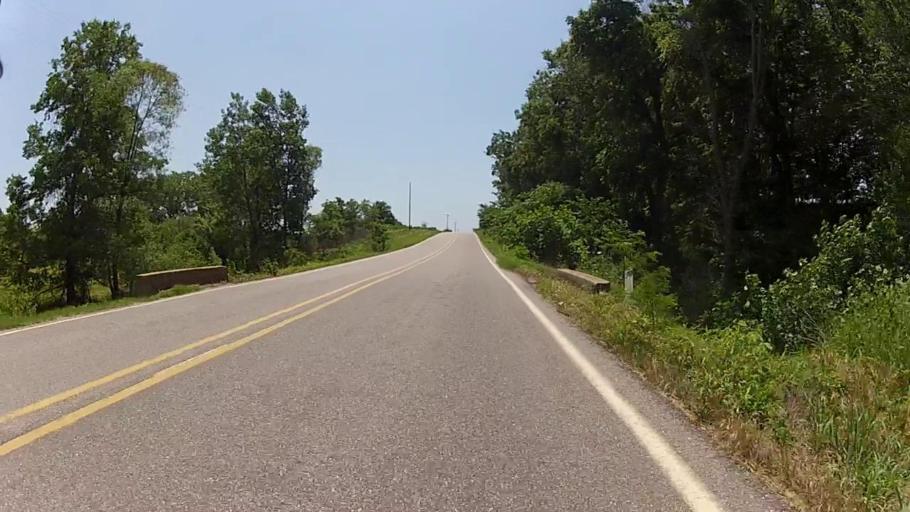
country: US
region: Kansas
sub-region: Montgomery County
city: Cherryvale
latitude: 37.2403
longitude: -95.5376
